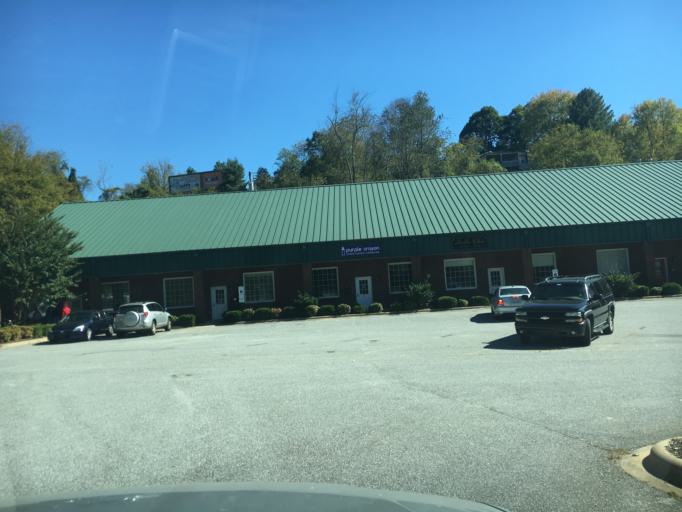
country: US
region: North Carolina
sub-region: Buncombe County
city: Woodfin
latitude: 35.6233
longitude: -82.5768
